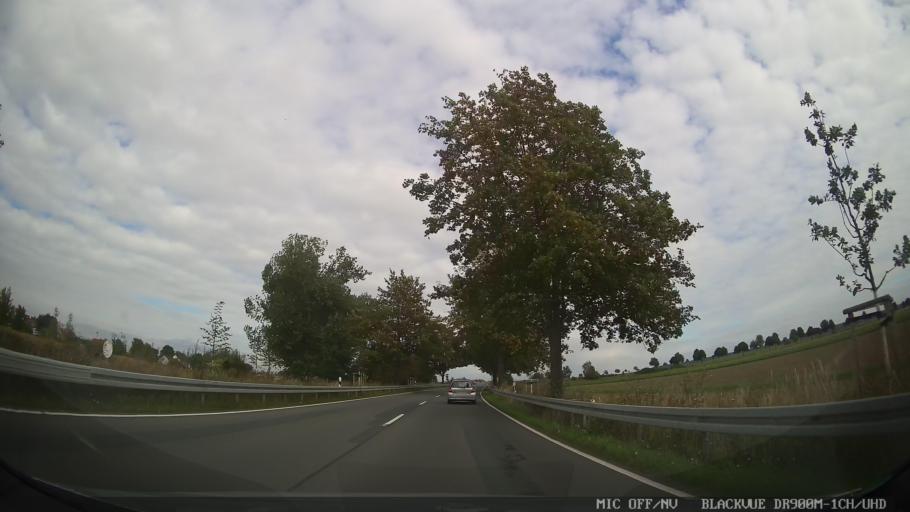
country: DE
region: Lower Saxony
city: Cramme
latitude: 52.1172
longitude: 10.4284
